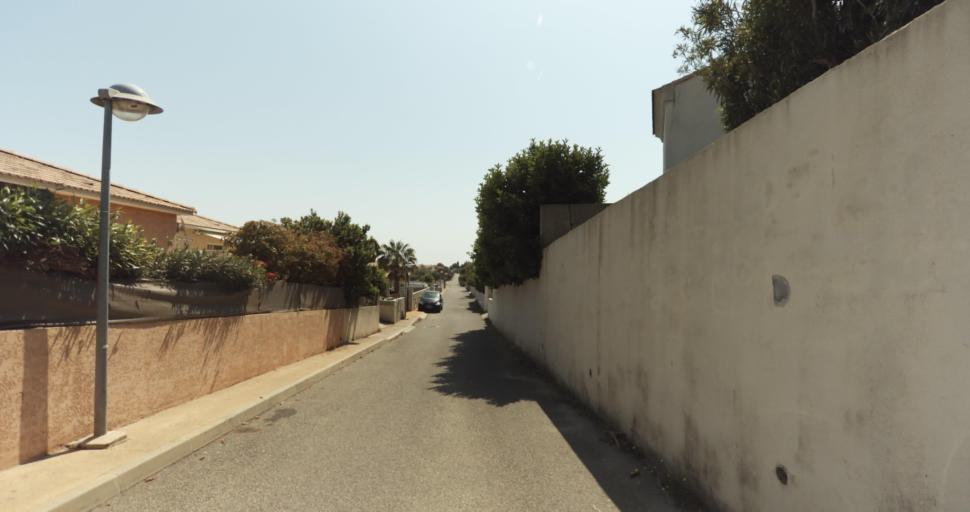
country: FR
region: Corsica
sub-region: Departement de la Haute-Corse
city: Biguglia
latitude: 42.6139
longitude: 9.4278
